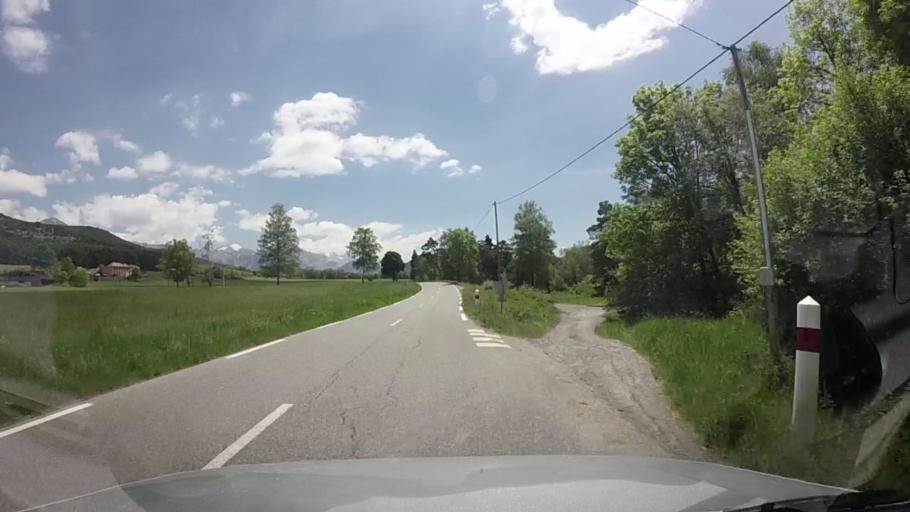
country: FR
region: Provence-Alpes-Cote d'Azur
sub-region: Departement des Alpes-de-Haute-Provence
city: Seyne-les-Alpes
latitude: 44.3636
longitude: 6.3258
